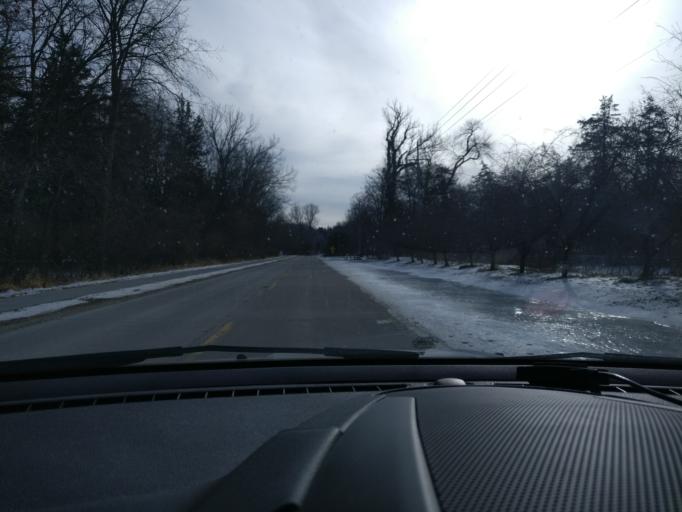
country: US
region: Nebraska
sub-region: Dodge County
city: Fremont
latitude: 41.4160
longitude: -96.5216
